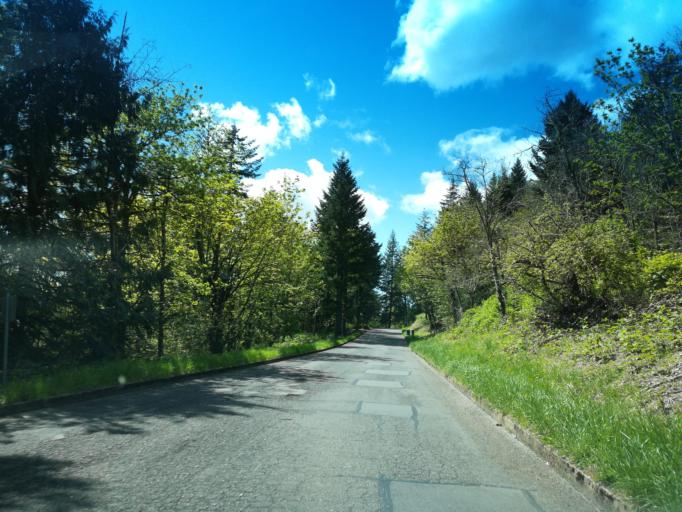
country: US
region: Oregon
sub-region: Multnomah County
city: Gresham
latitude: 45.4543
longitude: -122.4244
